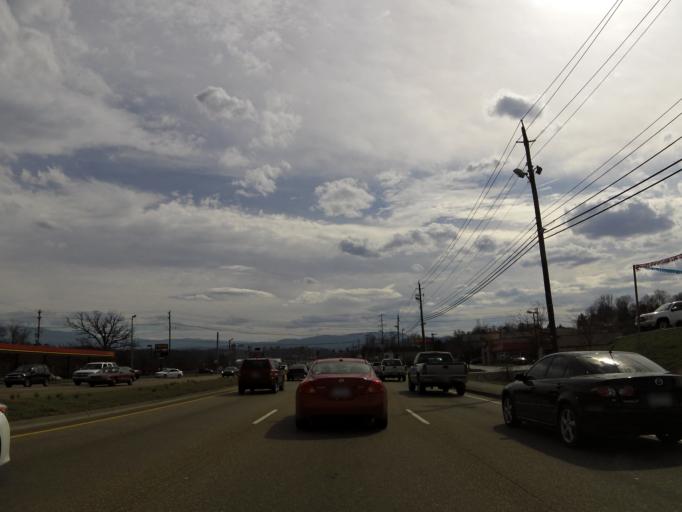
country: US
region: Tennessee
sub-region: Sevier County
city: Sevierville
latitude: 35.8443
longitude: -83.5707
